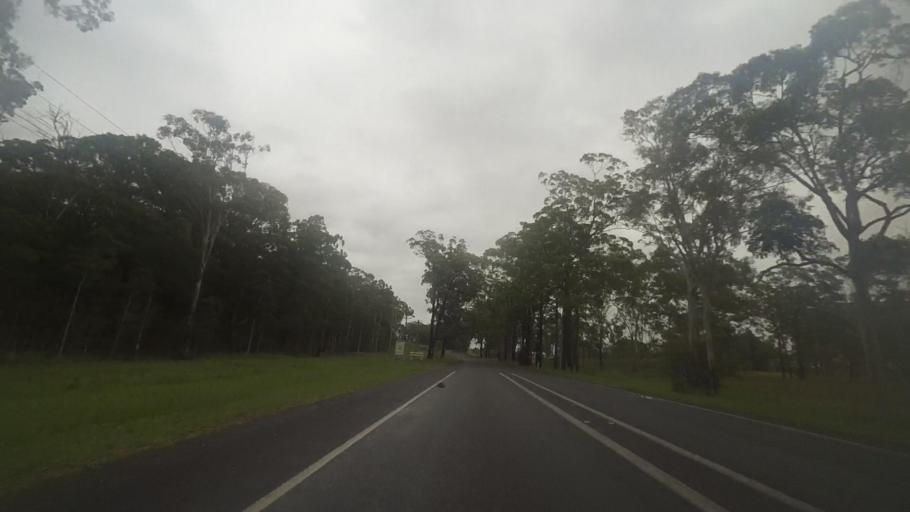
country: AU
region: New South Wales
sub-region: Port Stephens Shire
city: Port Stephens
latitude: -32.6485
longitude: 151.9766
